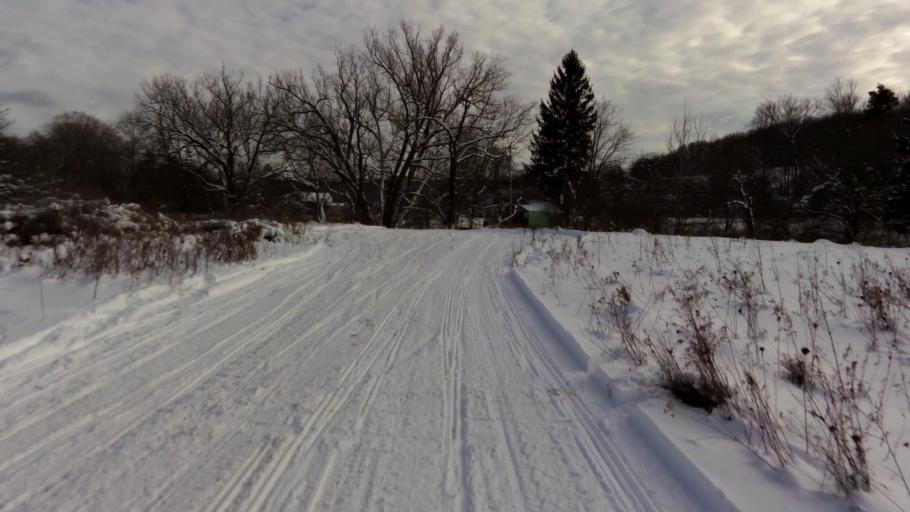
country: US
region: New York
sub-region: Cattaraugus County
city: Franklinville
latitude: 42.3383
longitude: -78.4724
